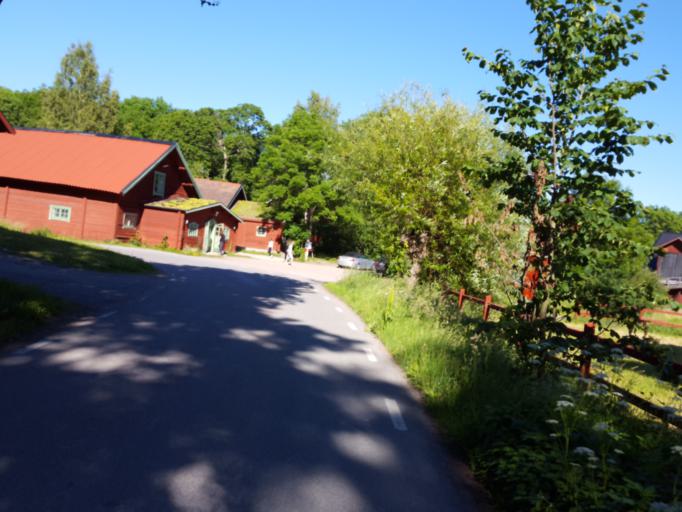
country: SE
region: Uppsala
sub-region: Uppsala Kommun
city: Alsike
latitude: 59.8195
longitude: 17.7818
